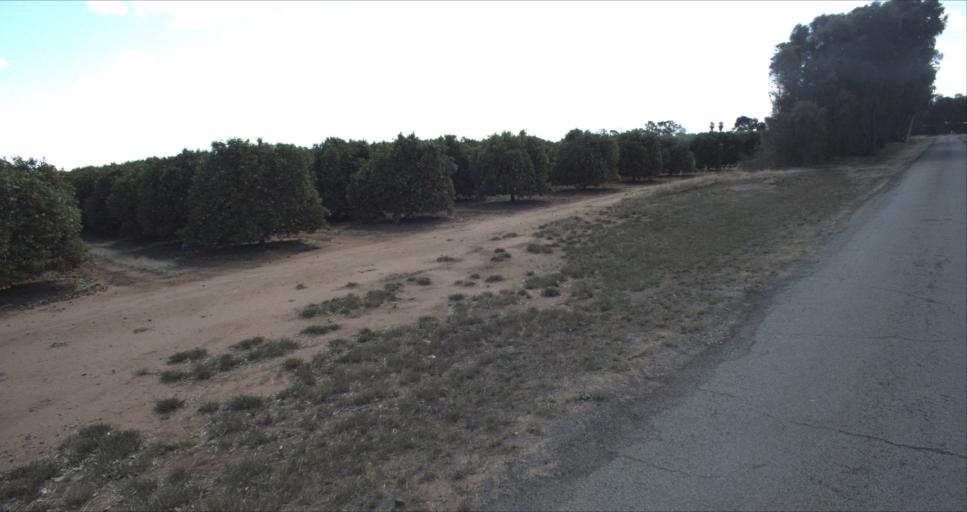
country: AU
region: New South Wales
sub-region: Leeton
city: Leeton
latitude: -34.5131
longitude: 146.2326
